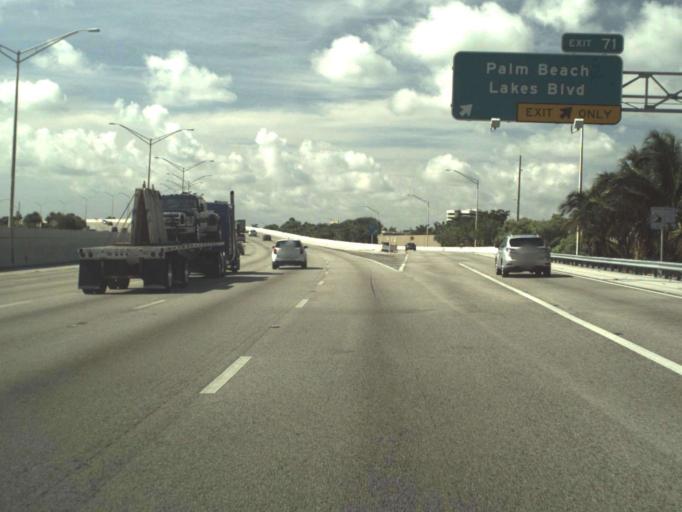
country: US
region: Florida
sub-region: Palm Beach County
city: Schall Circle
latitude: 26.7237
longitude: -80.0917
